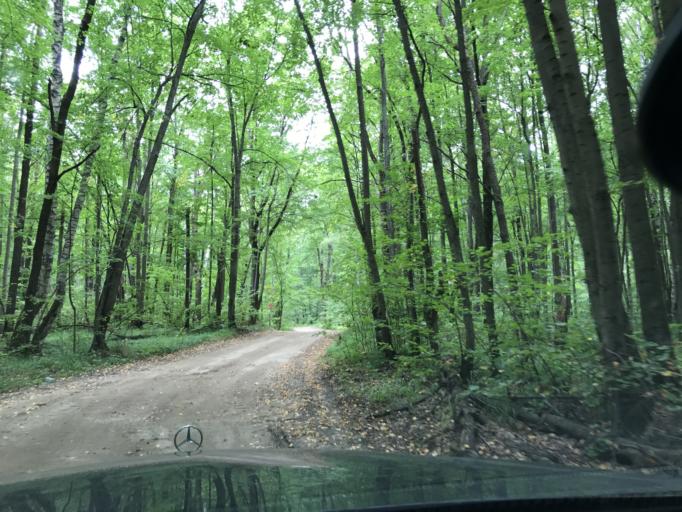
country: RU
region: Nizjnij Novgorod
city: Vacha
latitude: 55.9884
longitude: 42.8091
